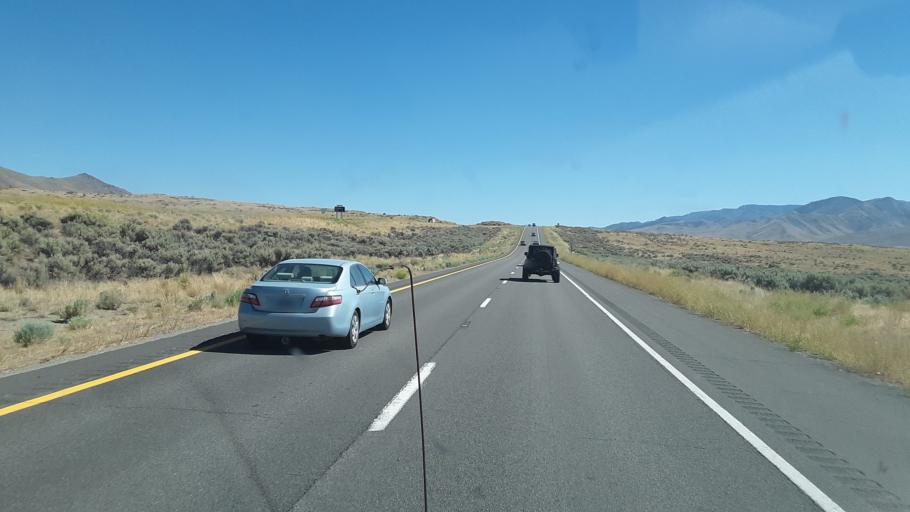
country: US
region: Nevada
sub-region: Washoe County
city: Cold Springs
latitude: 39.7663
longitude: -120.0391
